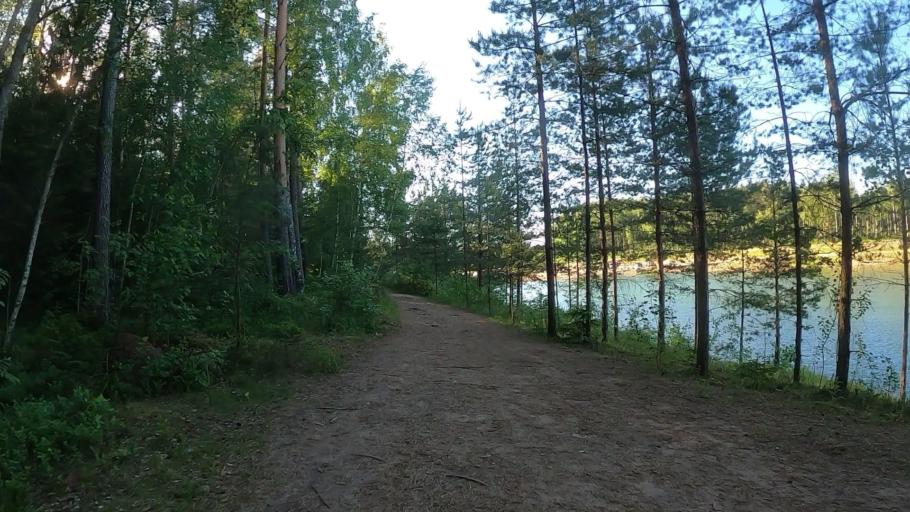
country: LV
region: Ikskile
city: Ikskile
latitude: 56.8409
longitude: 24.5477
